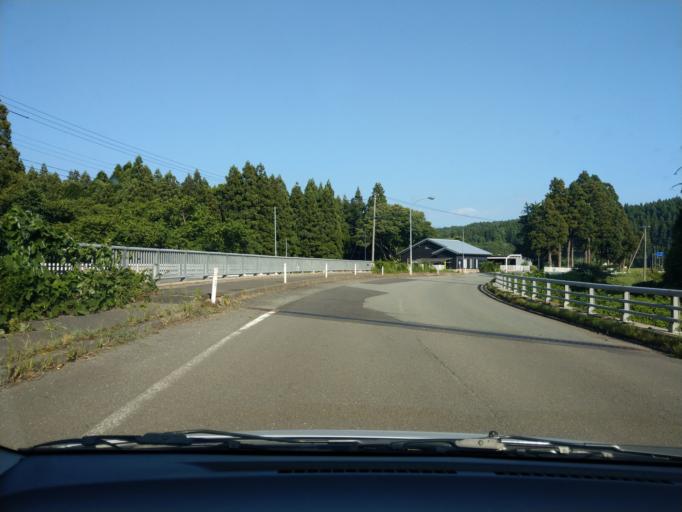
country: JP
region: Akita
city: Akita
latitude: 39.6006
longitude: 140.2108
